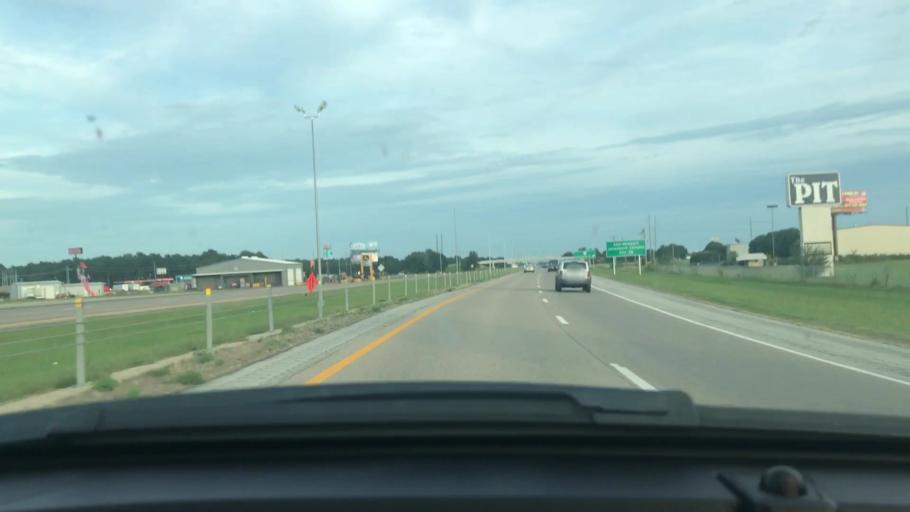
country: US
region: Arkansas
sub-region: Craighead County
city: Jonesboro
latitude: 35.8058
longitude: -90.6307
